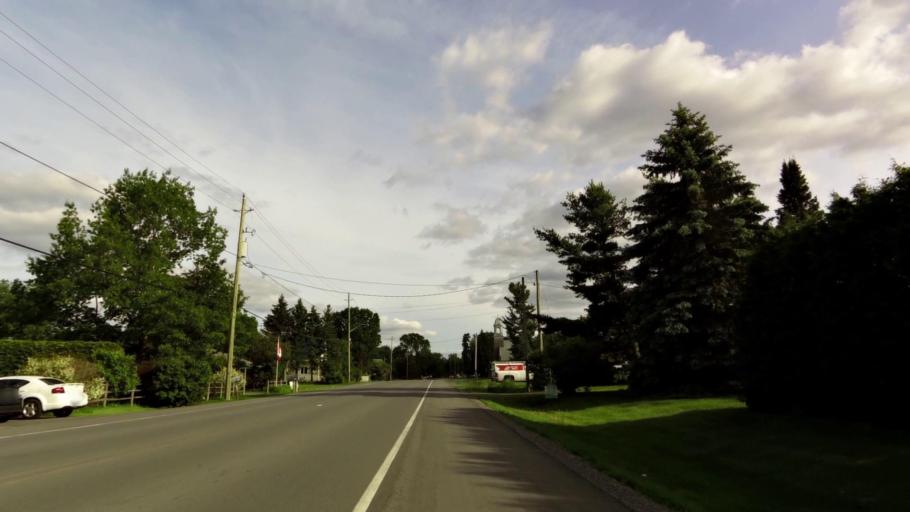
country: CA
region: Ontario
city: Ottawa
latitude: 45.2007
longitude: -75.5683
